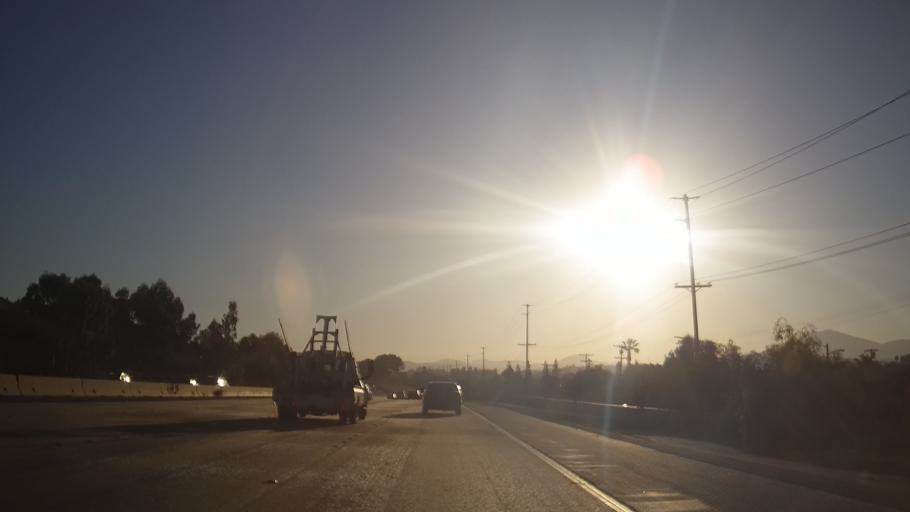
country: US
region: California
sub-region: San Diego County
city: Lemon Grove
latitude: 32.7447
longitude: -117.0423
